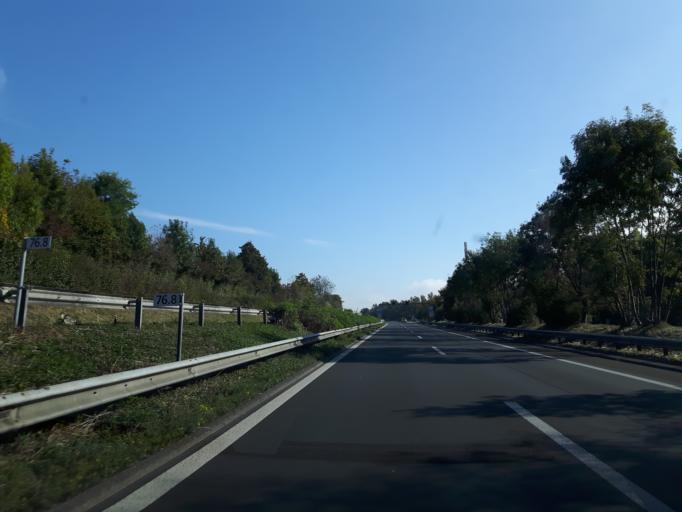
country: CH
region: Lucerne
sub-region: Sursee District
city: Eich
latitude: 47.1564
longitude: 8.1567
